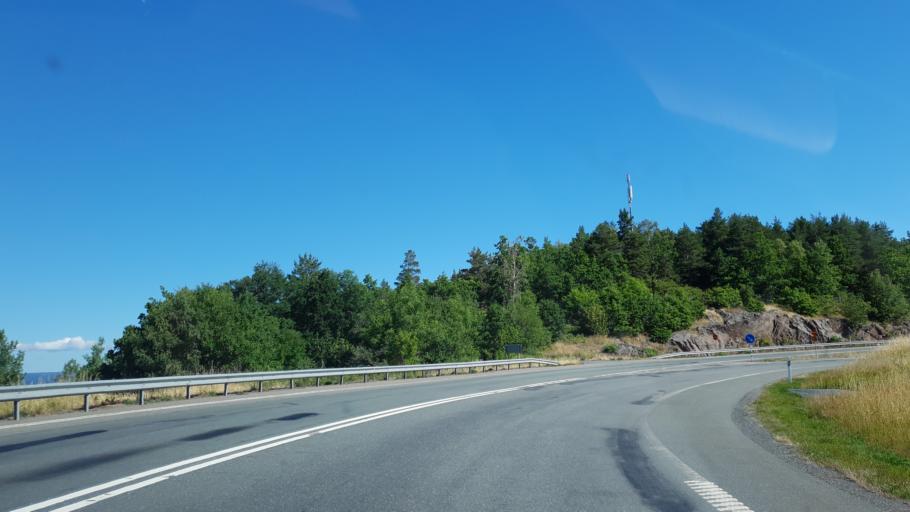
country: SE
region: Joenkoeping
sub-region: Jonkopings Kommun
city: Kaxholmen
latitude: 57.9255
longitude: 14.3172
